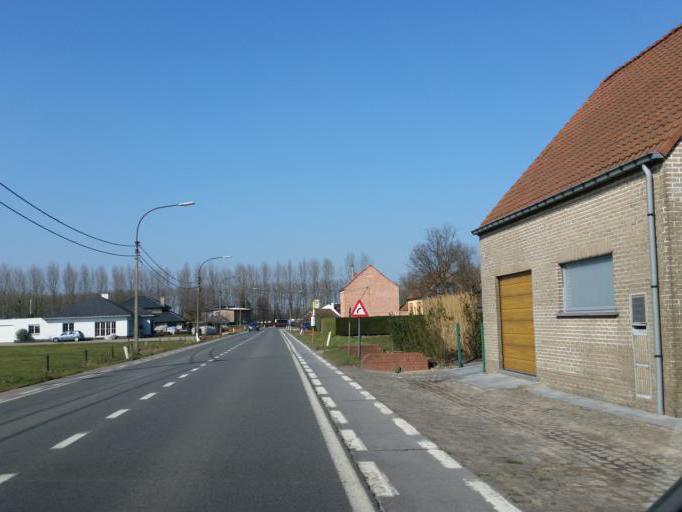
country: BE
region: Flanders
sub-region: Provincie Oost-Vlaanderen
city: Wachtebeke
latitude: 51.1456
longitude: 3.8658
